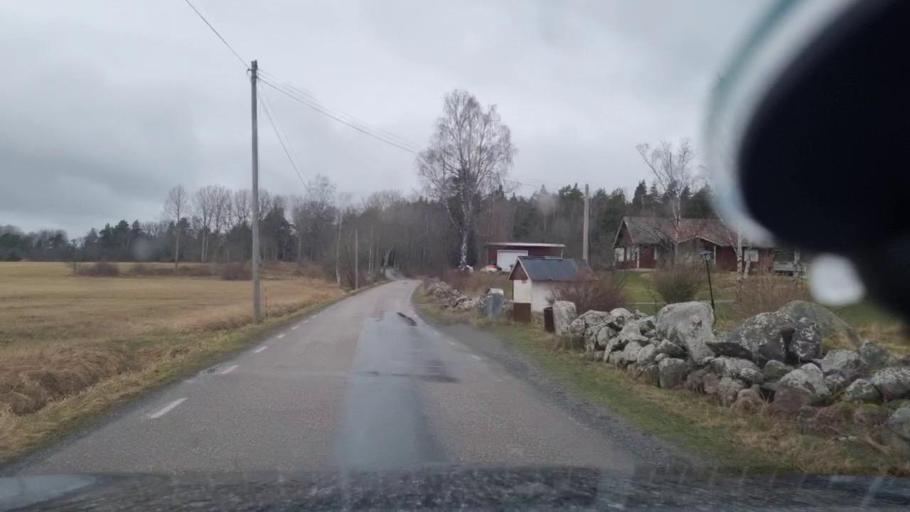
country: SE
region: Stockholm
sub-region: Taby Kommun
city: Taby
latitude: 59.4838
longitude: 18.0146
